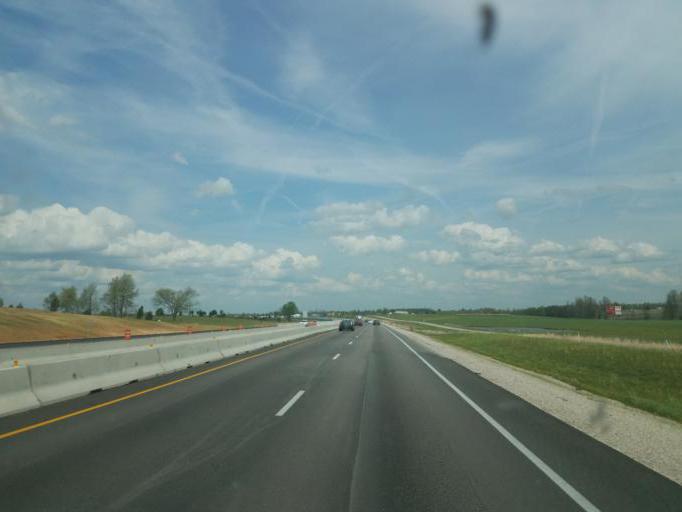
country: US
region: Kentucky
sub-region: Larue County
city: Hodgenville
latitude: 37.4867
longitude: -85.8805
